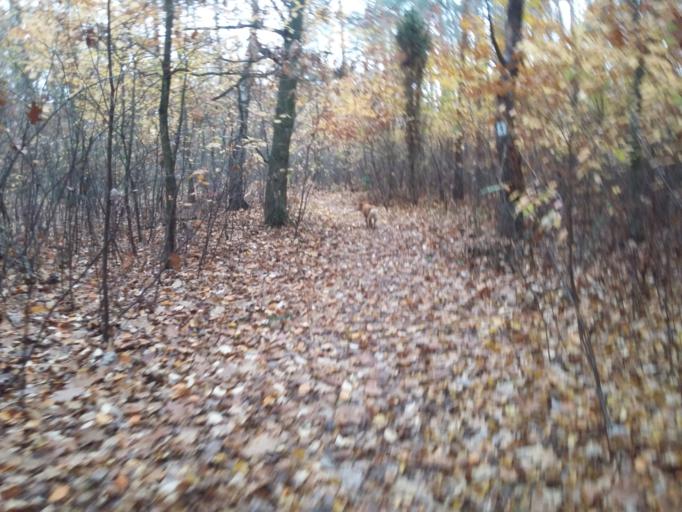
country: PL
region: Lodz Voivodeship
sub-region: Powiat pabianicki
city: Ksawerow
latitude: 51.7216
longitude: 19.3796
